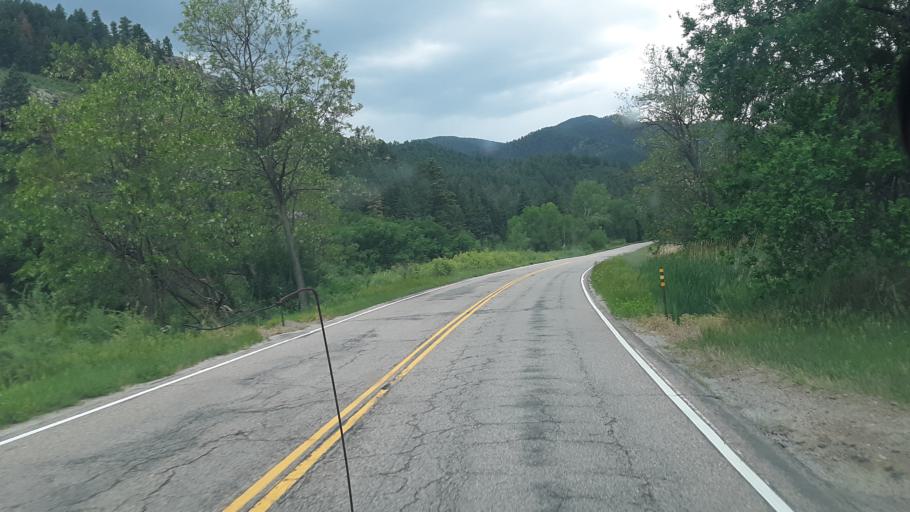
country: US
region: Colorado
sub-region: Fremont County
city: Florence
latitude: 38.1805
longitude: -105.1102
